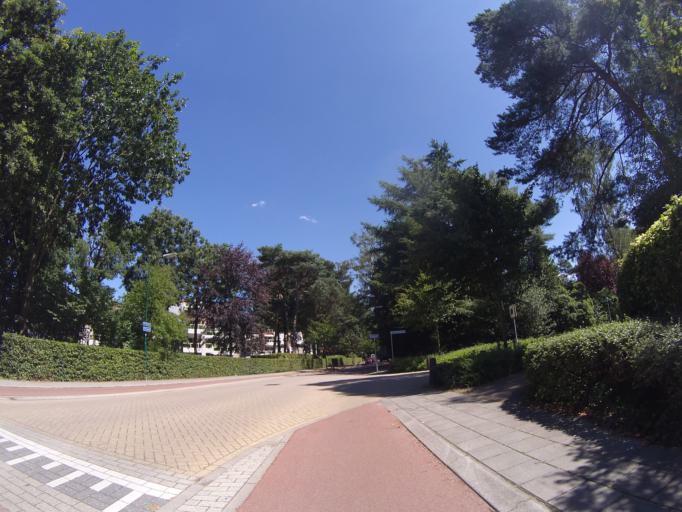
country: NL
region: Utrecht
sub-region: Gemeente Zeist
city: Zeist
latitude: 52.1356
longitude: 5.2275
